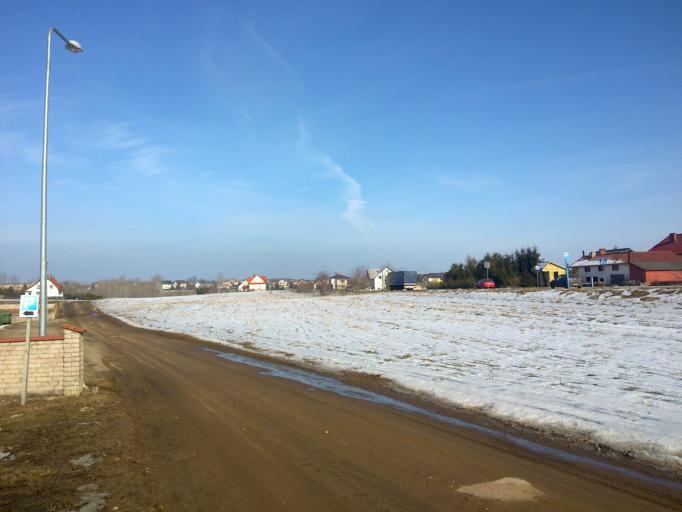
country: PL
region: Pomeranian Voivodeship
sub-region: Powiat bytowski
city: Lipnica
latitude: 53.9880
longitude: 17.3993
